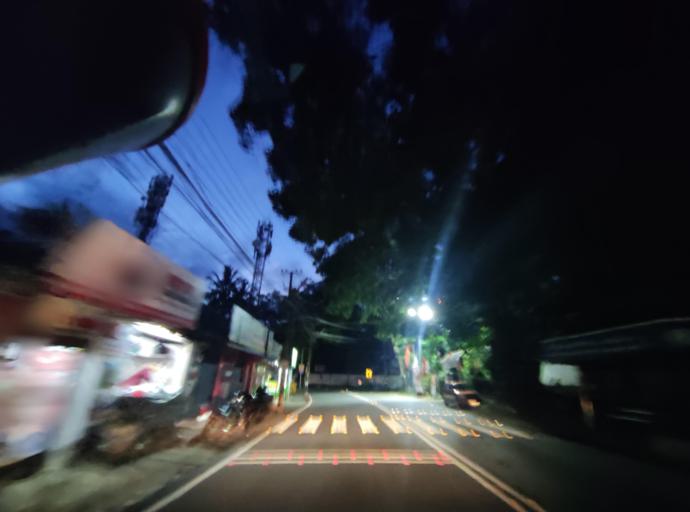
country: IN
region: Kerala
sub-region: Thiruvananthapuram
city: Thiruvananthapuram
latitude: 8.5430
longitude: 76.9609
